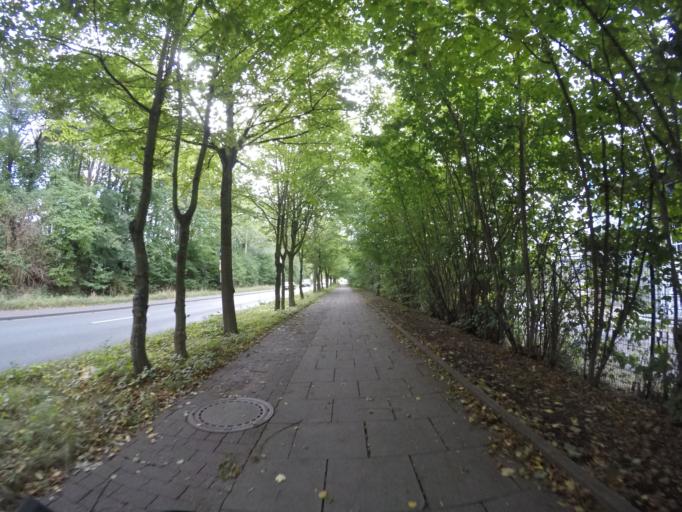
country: DE
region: North Rhine-Westphalia
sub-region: Regierungsbezirk Detmold
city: Herford
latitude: 52.1272
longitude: 8.6662
